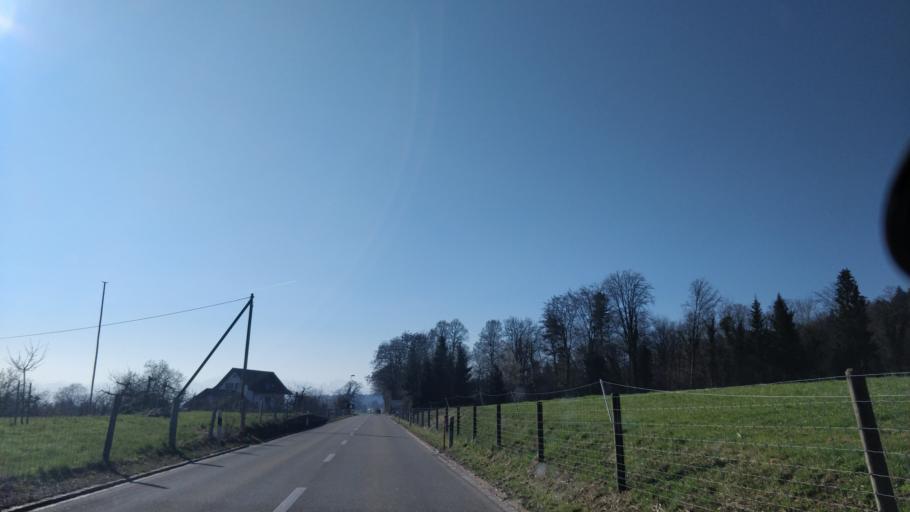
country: CH
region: Zurich
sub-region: Bezirk Uster
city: Ebmatingen
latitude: 47.3533
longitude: 8.6599
